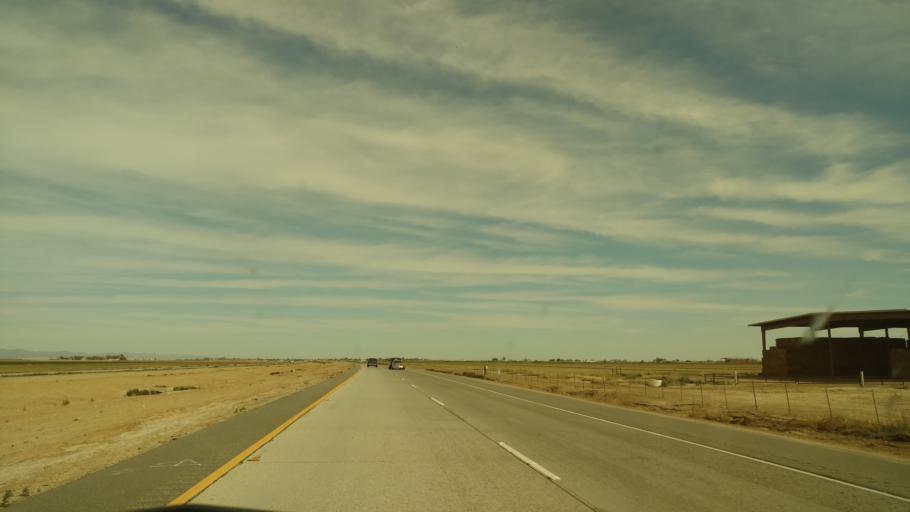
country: US
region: California
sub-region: Imperial County
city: Westmorland
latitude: 33.0373
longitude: -115.6821
